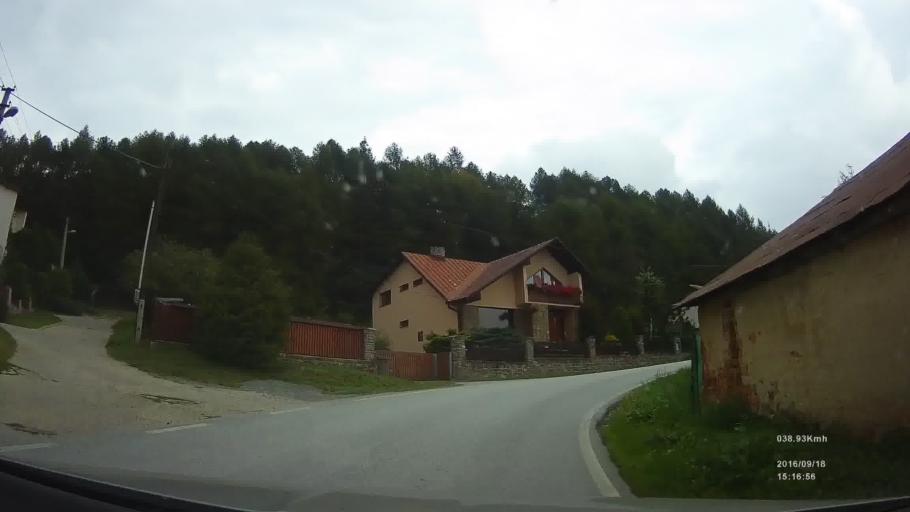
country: SK
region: Presovsky
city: Lubica
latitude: 49.0222
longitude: 20.4863
